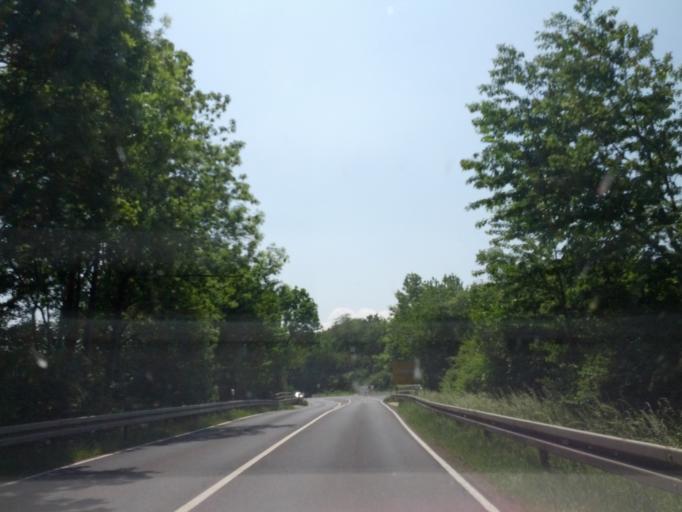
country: DE
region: Thuringia
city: Empfertshausen
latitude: 50.6701
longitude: 10.1154
